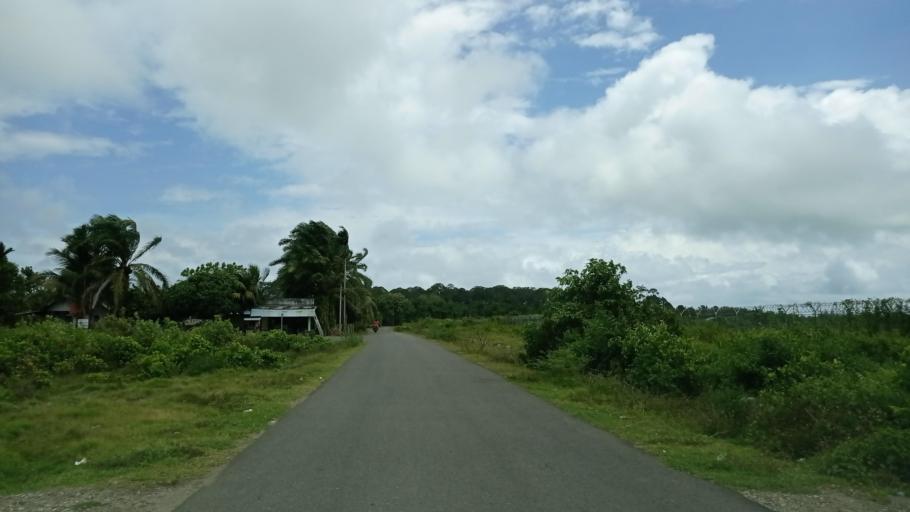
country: ID
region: Jambi
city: Sungai Penuh
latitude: -2.5468
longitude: 101.0938
